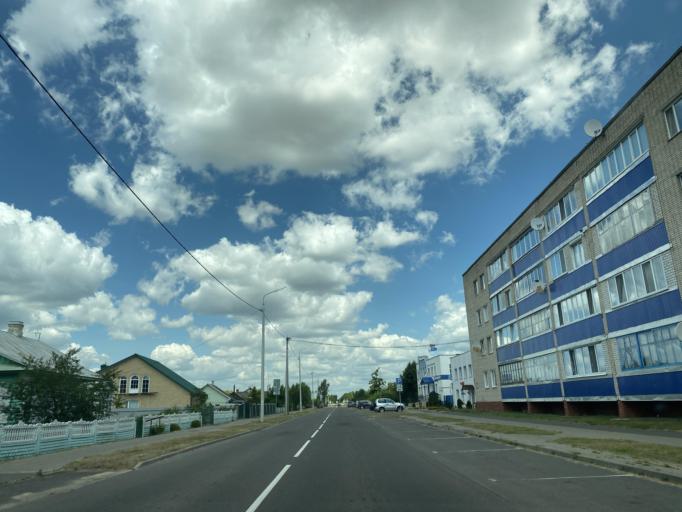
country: BY
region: Brest
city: Ivanava
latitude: 52.1513
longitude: 25.5428
